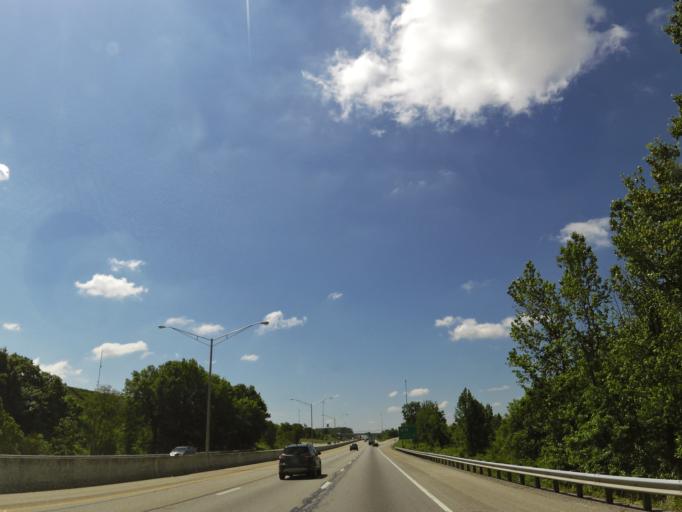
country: US
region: Kentucky
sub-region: Laurel County
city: London
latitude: 37.1524
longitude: -84.1126
